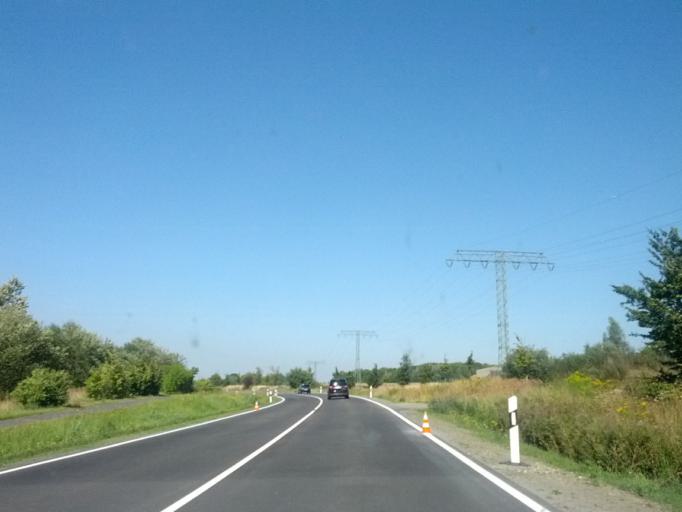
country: DE
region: Mecklenburg-Vorpommern
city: Sagard
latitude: 54.4951
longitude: 13.5737
